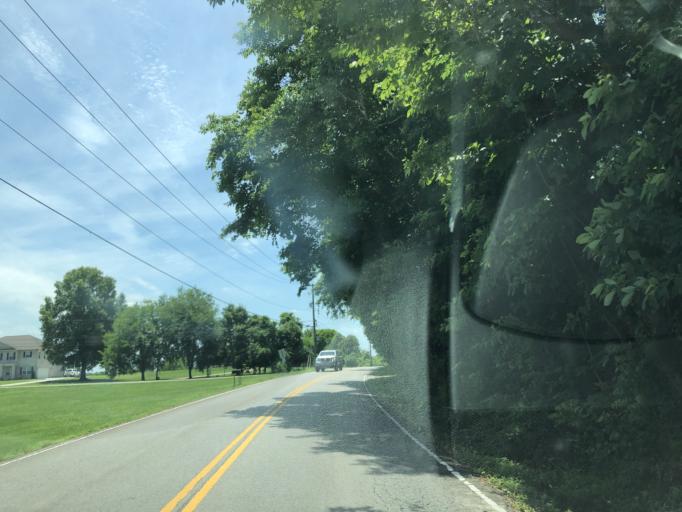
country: US
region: Tennessee
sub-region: Williamson County
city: Nolensville
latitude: 36.0326
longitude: -86.6614
